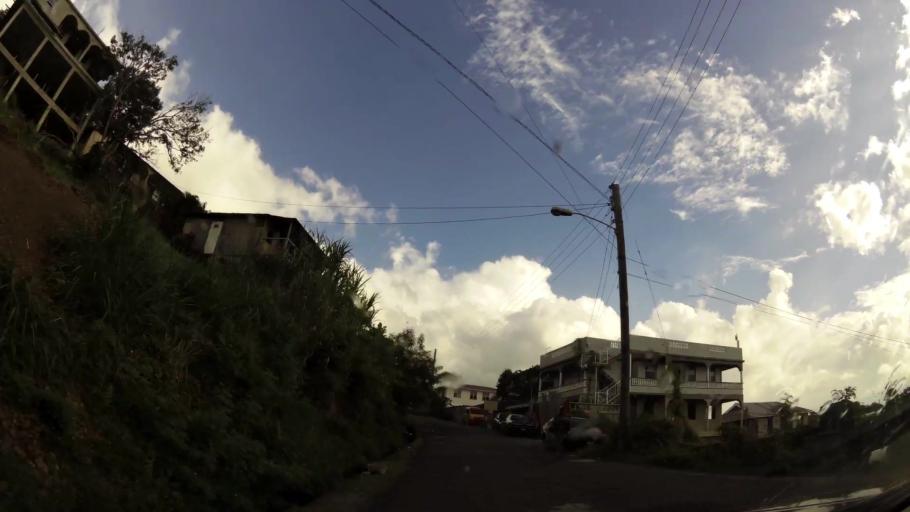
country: DM
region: Saint George
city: Roseau
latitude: 15.3090
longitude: -61.3877
